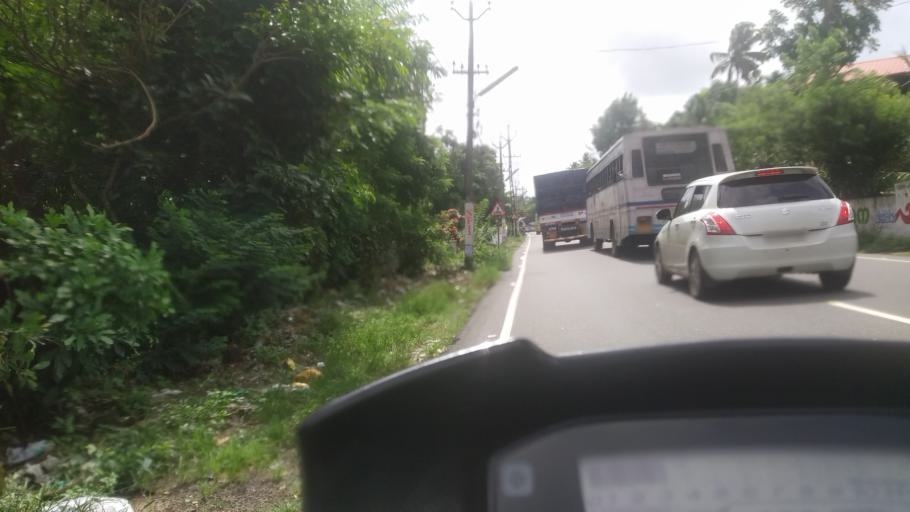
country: IN
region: Kerala
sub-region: Ernakulam
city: Elur
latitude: 10.1340
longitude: 76.2741
